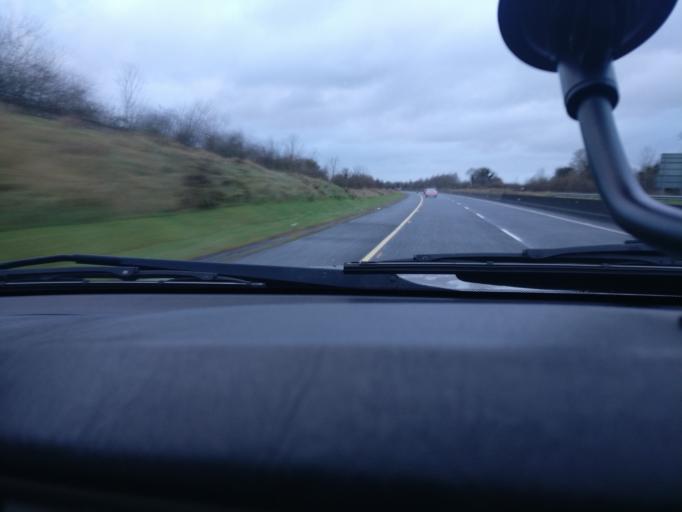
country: IE
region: Leinster
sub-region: An Iarmhi
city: Kilbeggan
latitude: 53.3672
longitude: -7.5311
